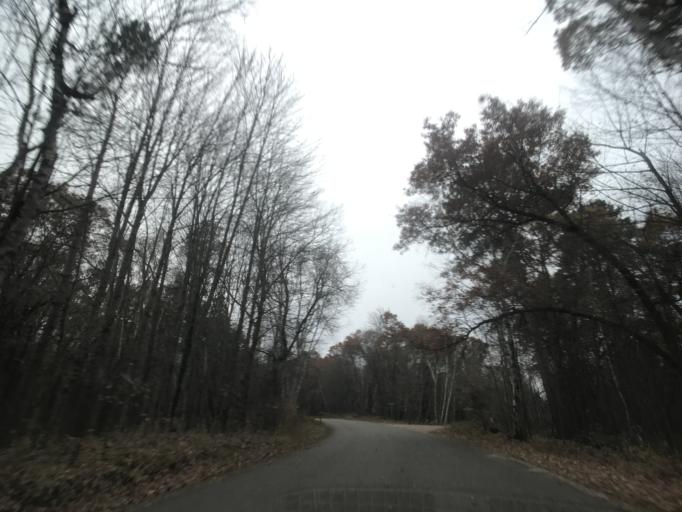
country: US
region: Michigan
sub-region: Dickinson County
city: Kingsford
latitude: 45.3796
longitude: -88.3219
